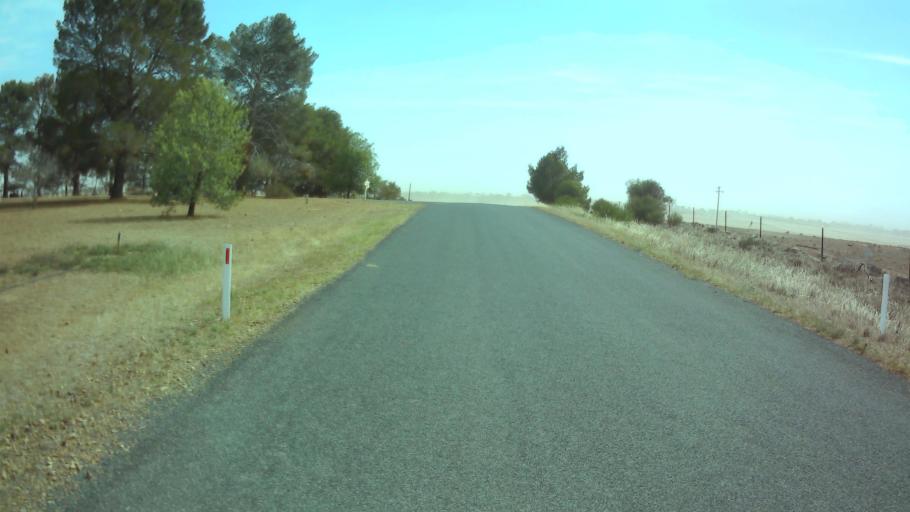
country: AU
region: New South Wales
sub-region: Weddin
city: Grenfell
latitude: -33.7306
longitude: 147.9980
